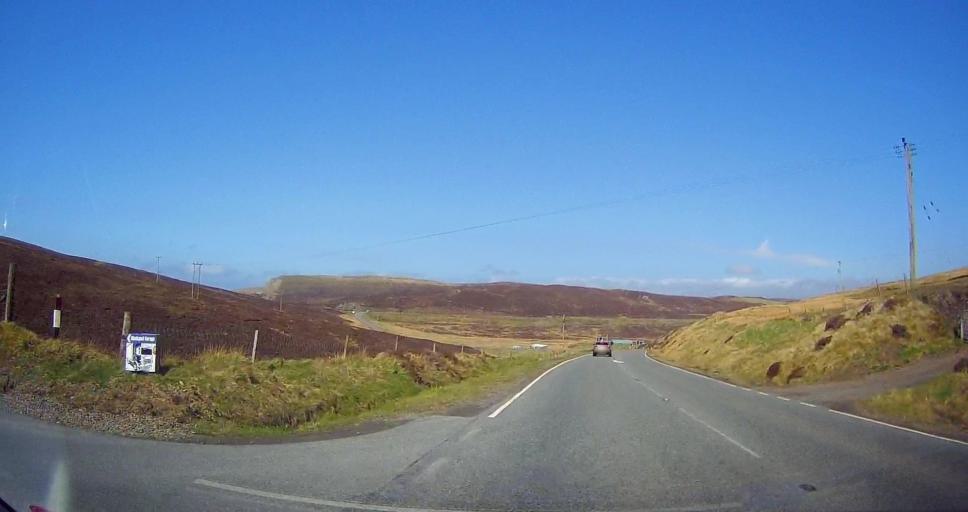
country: GB
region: Scotland
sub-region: Shetland Islands
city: Lerwick
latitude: 60.1381
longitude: -1.2333
